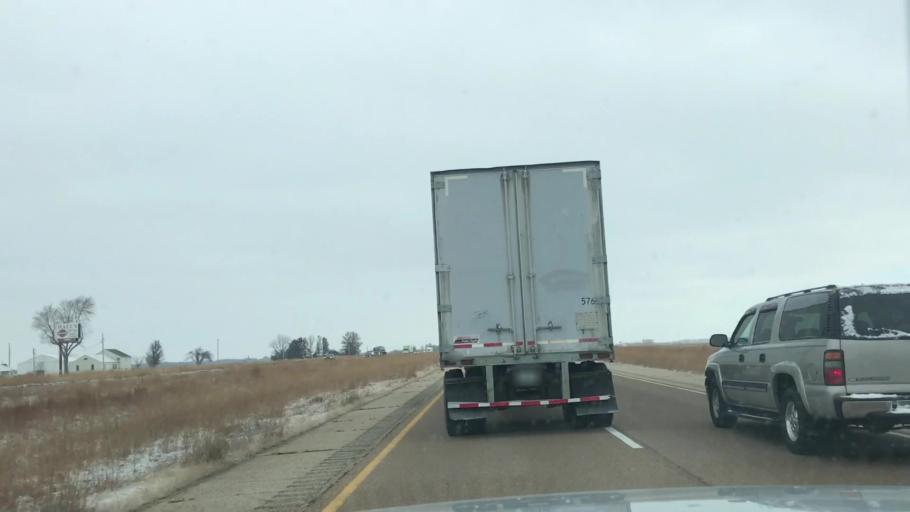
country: US
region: Illinois
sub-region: Montgomery County
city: Raymond
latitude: 39.3975
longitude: -89.6432
